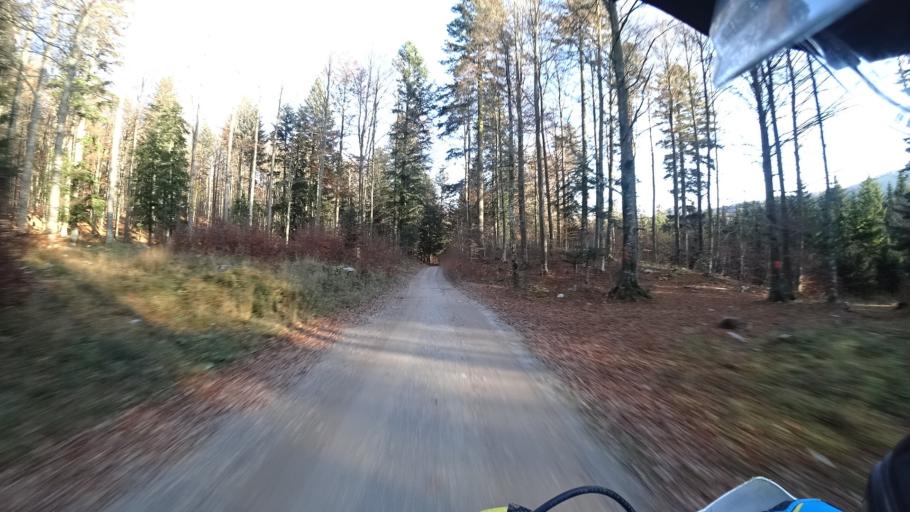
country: HR
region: Primorsko-Goranska
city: Drazice
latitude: 45.4824
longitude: 14.4716
